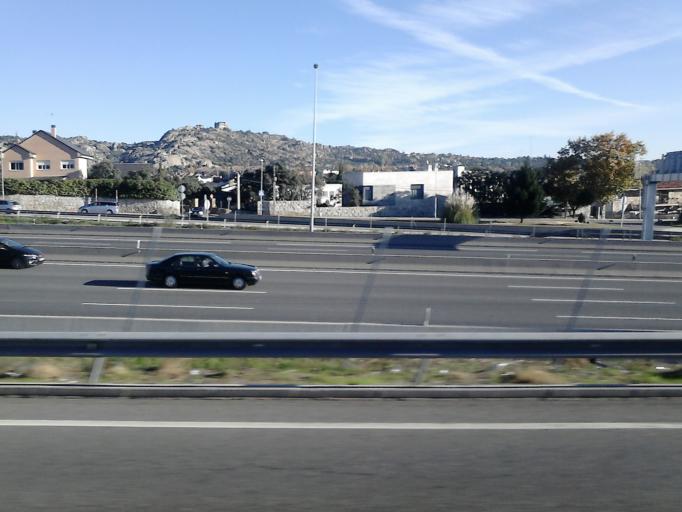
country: ES
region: Madrid
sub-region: Provincia de Madrid
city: Torrelodones
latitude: 40.5763
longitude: -3.9352
